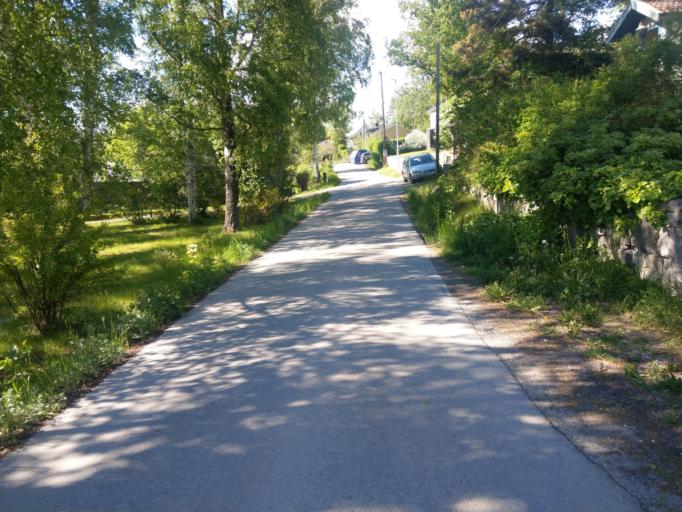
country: SE
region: Stockholm
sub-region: Jarfalla Kommun
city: Jakobsberg
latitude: 59.3920
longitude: 17.8563
